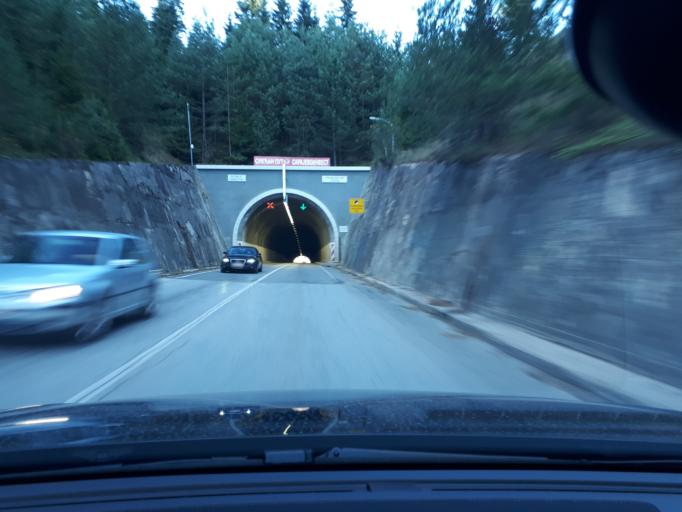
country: BA
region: Republika Srpska
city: Pale
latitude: 43.8277
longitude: 18.5590
